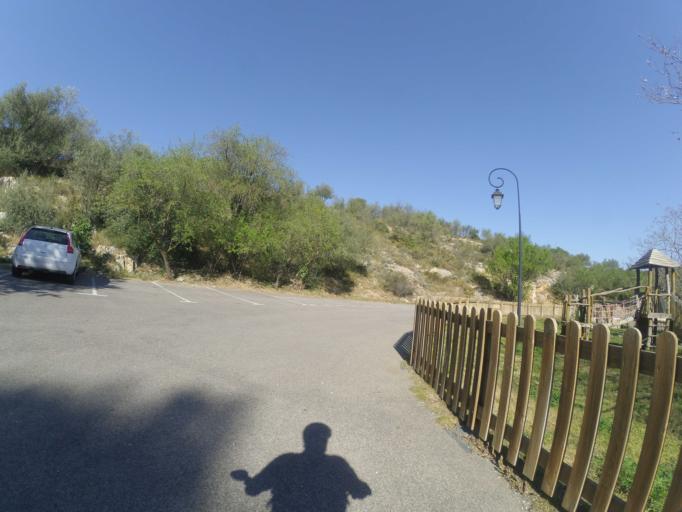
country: FR
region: Languedoc-Roussillon
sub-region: Departement des Pyrenees-Orientales
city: Baixas
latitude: 42.7596
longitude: 2.7532
